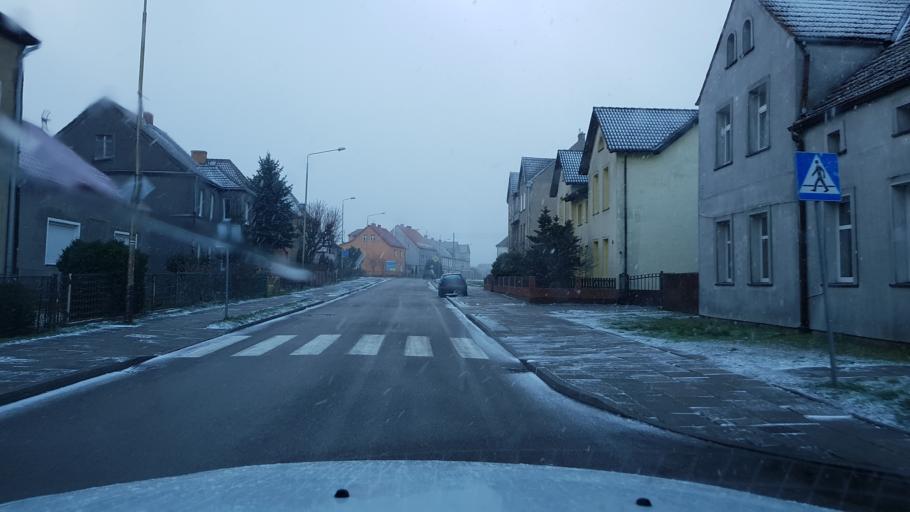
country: PL
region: West Pomeranian Voivodeship
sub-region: Powiat gryficki
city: Trzebiatow
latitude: 54.0587
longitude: 15.2794
